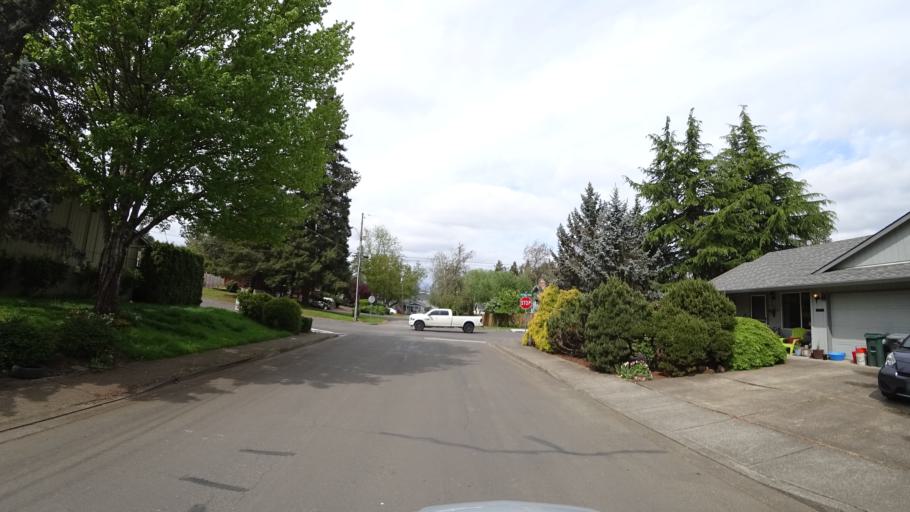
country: US
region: Oregon
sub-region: Washington County
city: Hillsboro
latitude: 45.5240
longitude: -122.9970
